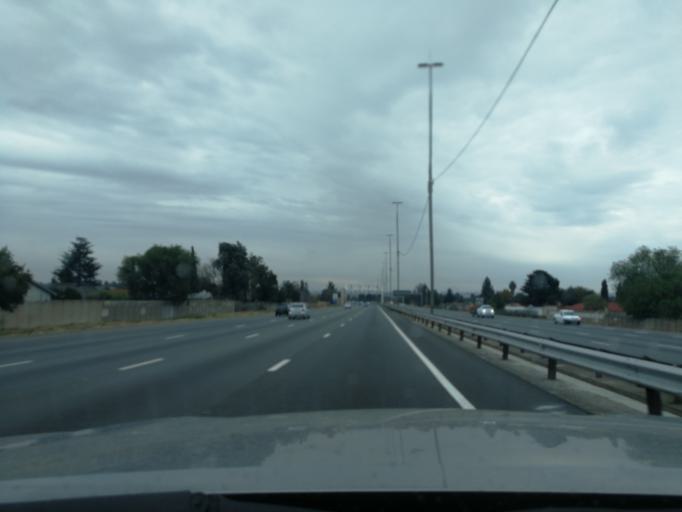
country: ZA
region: Gauteng
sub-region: Ekurhuleni Metropolitan Municipality
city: Germiston
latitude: -26.2708
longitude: 28.1498
